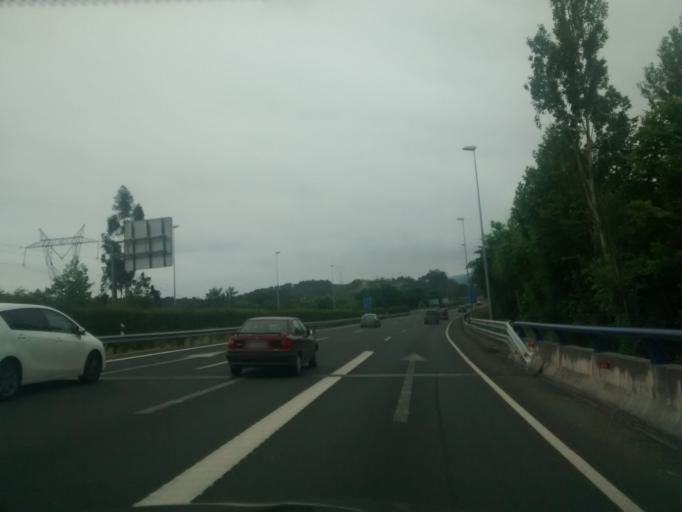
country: ES
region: Cantabria
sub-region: Provincia de Cantabria
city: Luzmela
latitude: 43.3256
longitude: -4.1882
